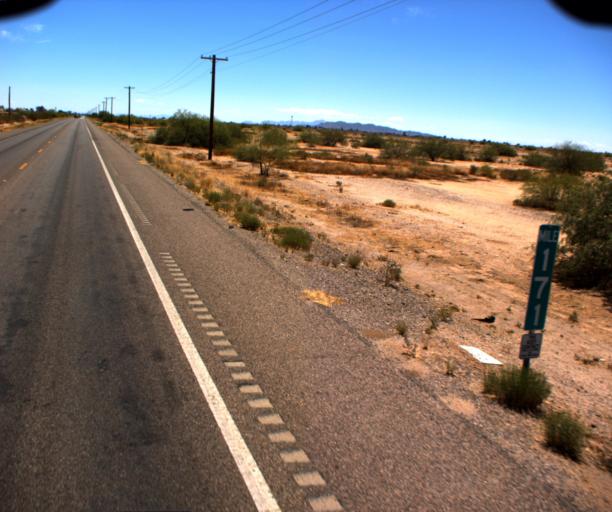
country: US
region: Arizona
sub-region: Pinal County
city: Casa Grande
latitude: 32.8795
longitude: -111.8770
